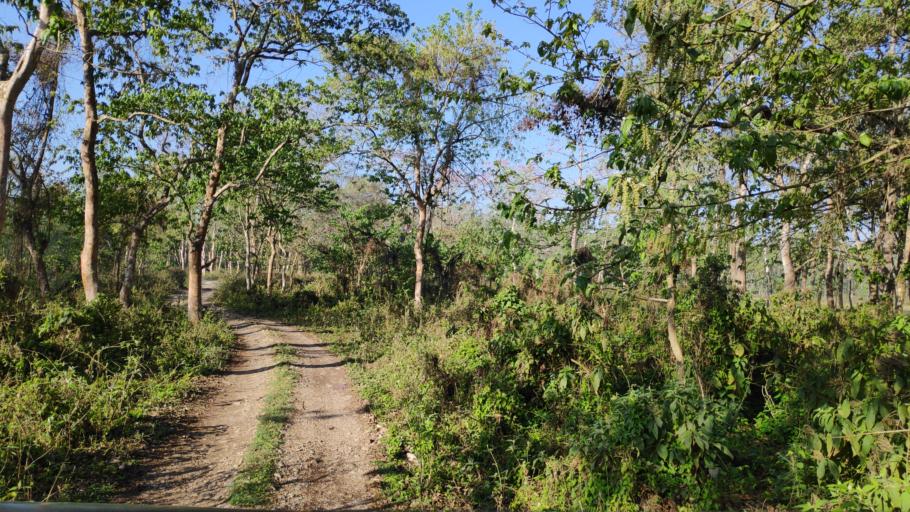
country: NP
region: Central Region
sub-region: Narayani Zone
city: Bharatpur
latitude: 27.5583
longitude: 84.5579
